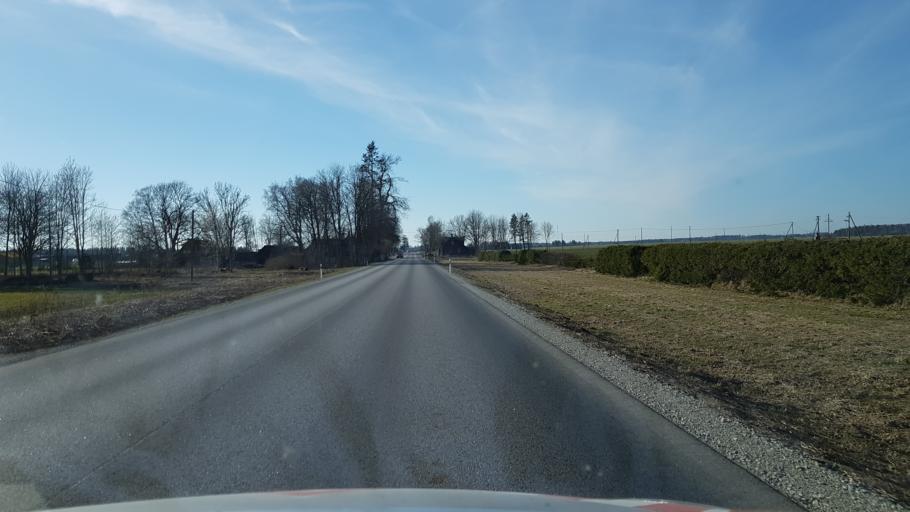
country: EE
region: Laeaene-Virumaa
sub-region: Vinni vald
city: Vinni
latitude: 59.2321
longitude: 26.5091
